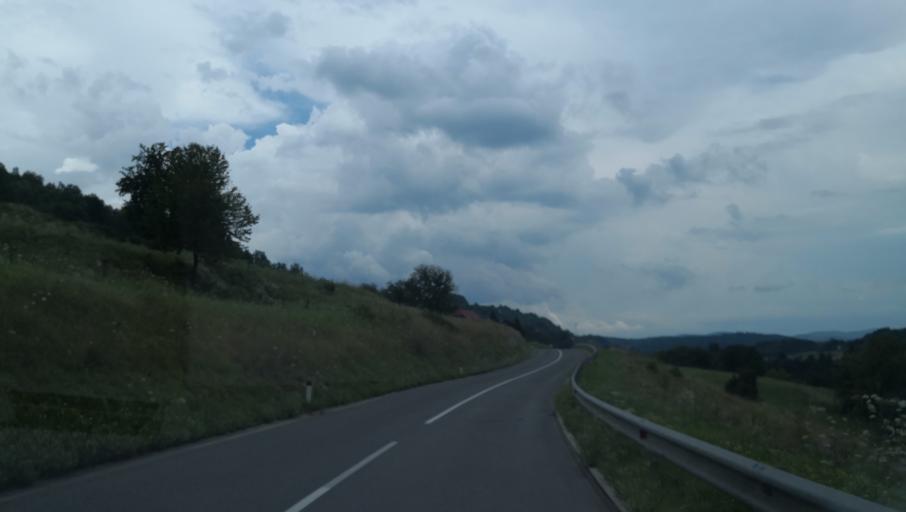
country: SI
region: Zuzemberk
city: Zuzemberk
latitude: 45.8577
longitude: 14.8658
